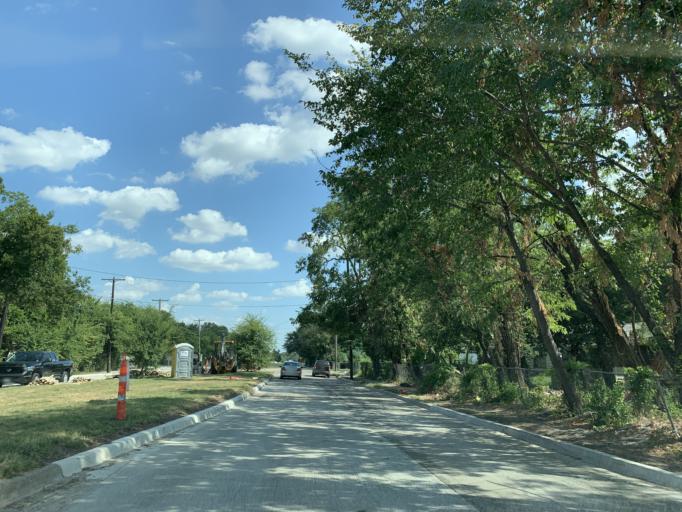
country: US
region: Texas
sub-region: Dallas County
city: Hutchins
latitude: 32.7010
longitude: -96.7766
